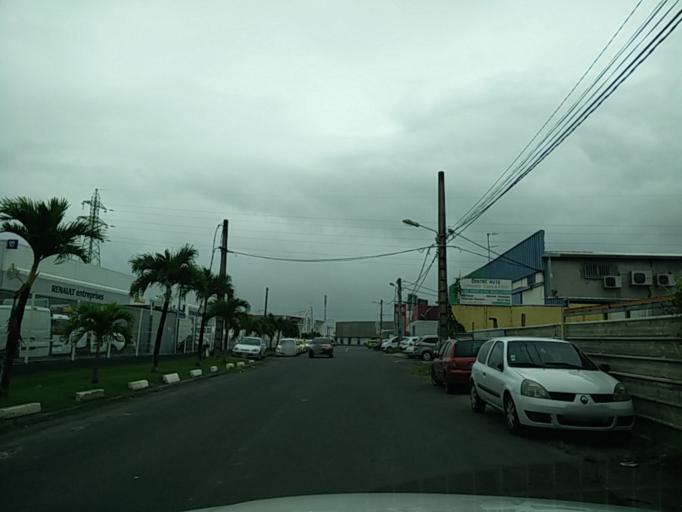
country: GP
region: Guadeloupe
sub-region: Guadeloupe
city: Pointe-a-Pitre
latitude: 16.2532
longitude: -61.5555
